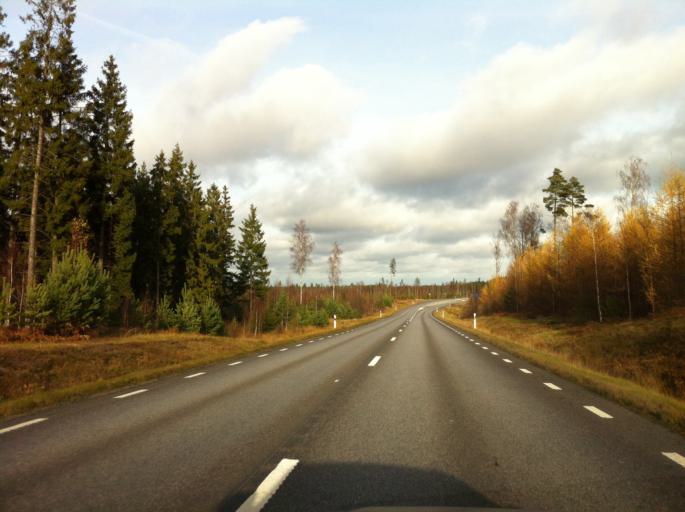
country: SE
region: Kronoberg
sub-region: Vaxjo Kommun
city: Gemla
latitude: 56.7791
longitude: 14.5789
